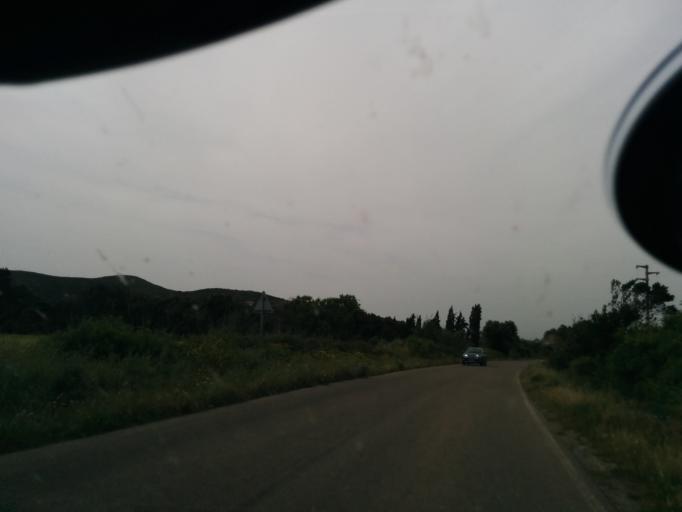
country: IT
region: Sardinia
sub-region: Provincia di Carbonia-Iglesias
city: Sant'Antioco
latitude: 39.0373
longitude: 8.4543
